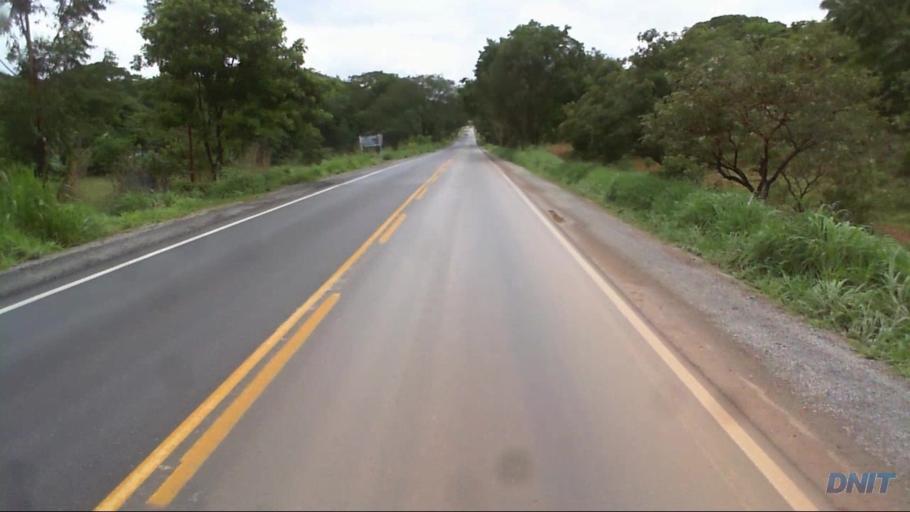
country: BR
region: Goias
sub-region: Padre Bernardo
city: Padre Bernardo
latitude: -15.5015
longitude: -48.2168
